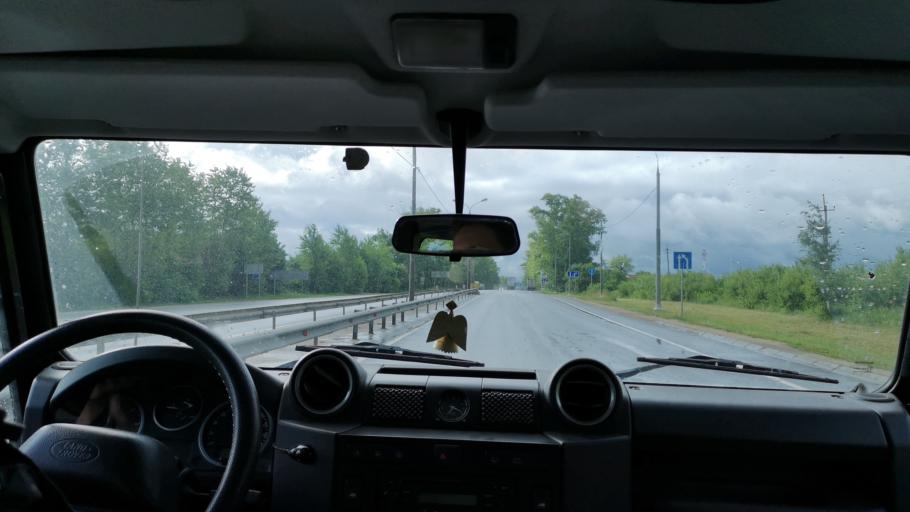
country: RU
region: Moskovskaya
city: Dmitrov
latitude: 56.3636
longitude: 37.4791
